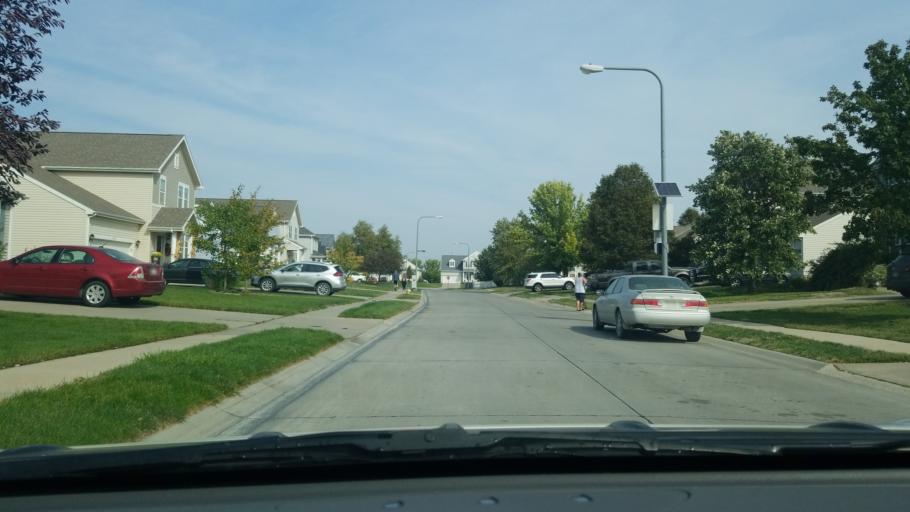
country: US
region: Nebraska
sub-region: Sarpy County
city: Papillion
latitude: 41.1304
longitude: -96.0567
